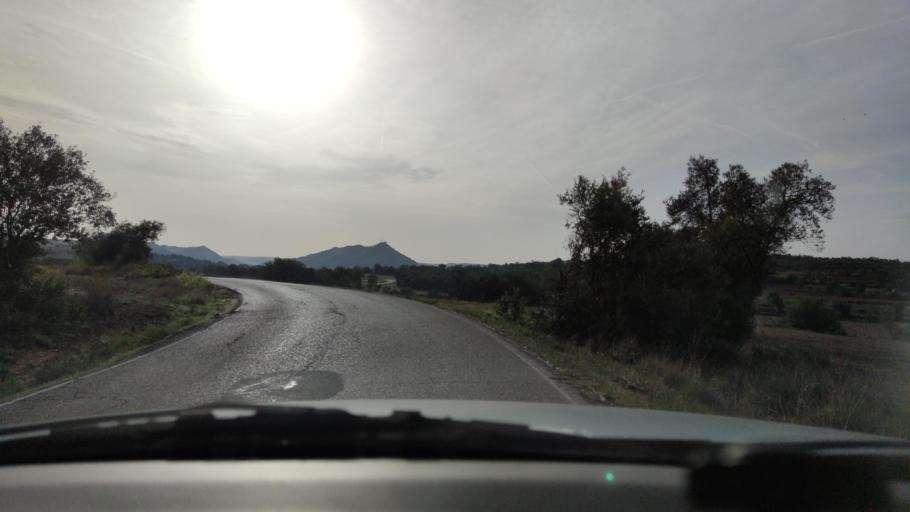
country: ES
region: Catalonia
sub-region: Provincia de Lleida
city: Artesa de Segre
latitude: 41.9119
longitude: 1.0319
